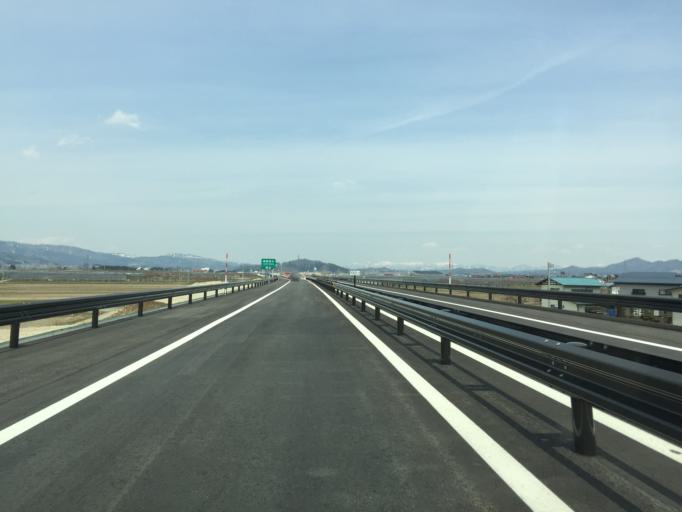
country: JP
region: Yamagata
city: Higashine
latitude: 38.4406
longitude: 140.3539
